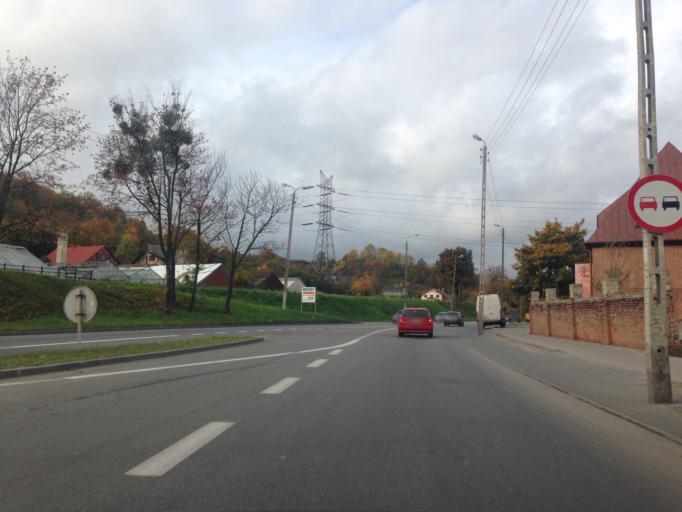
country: PL
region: Pomeranian Voivodeship
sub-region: Powiat gdanski
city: Pruszcz Gdanski
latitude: 54.2910
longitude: 18.6367
